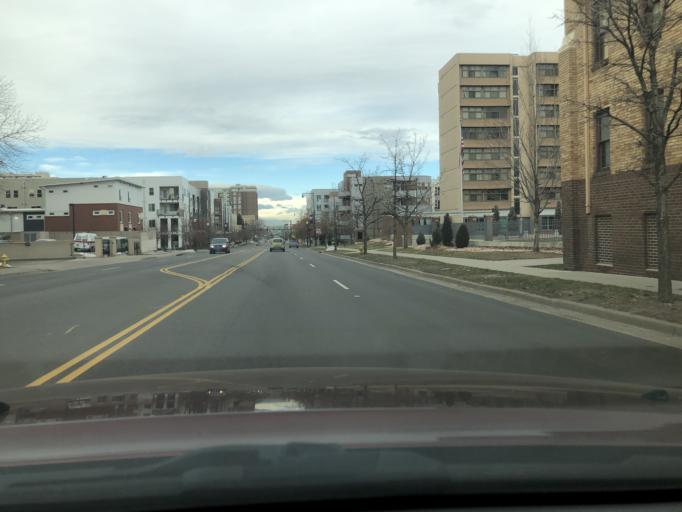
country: US
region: Colorado
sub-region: Denver County
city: Denver
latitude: 39.7479
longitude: -104.9787
